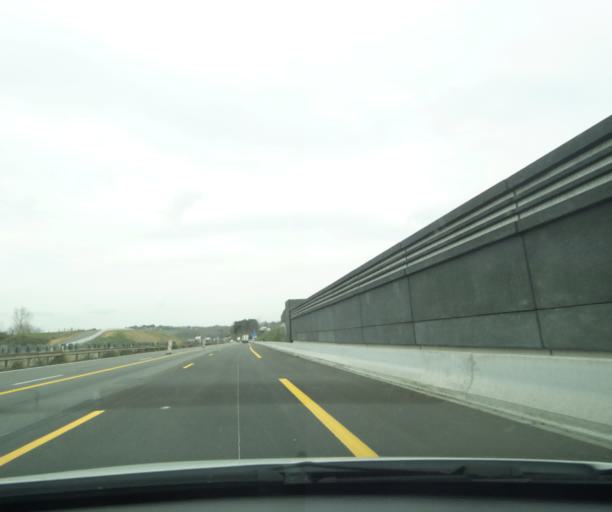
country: FR
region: Aquitaine
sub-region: Departement des Pyrenees-Atlantiques
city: Urrugne
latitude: 43.3585
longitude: -1.7076
